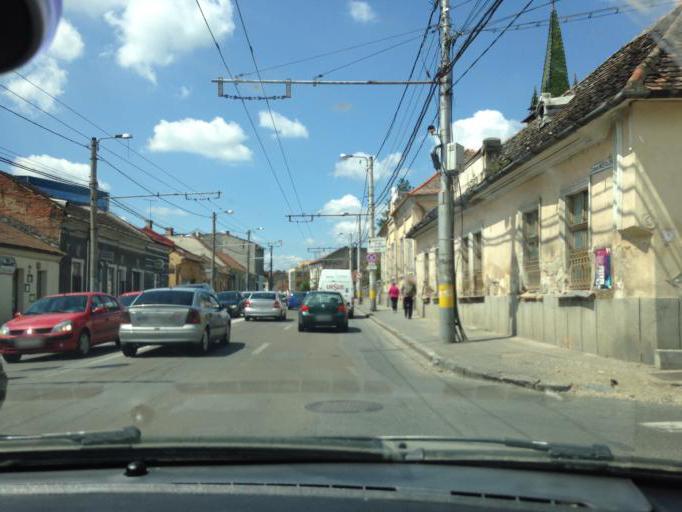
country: RO
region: Cluj
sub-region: Municipiul Cluj-Napoca
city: Cluj-Napoca
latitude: 46.7652
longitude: 23.5765
